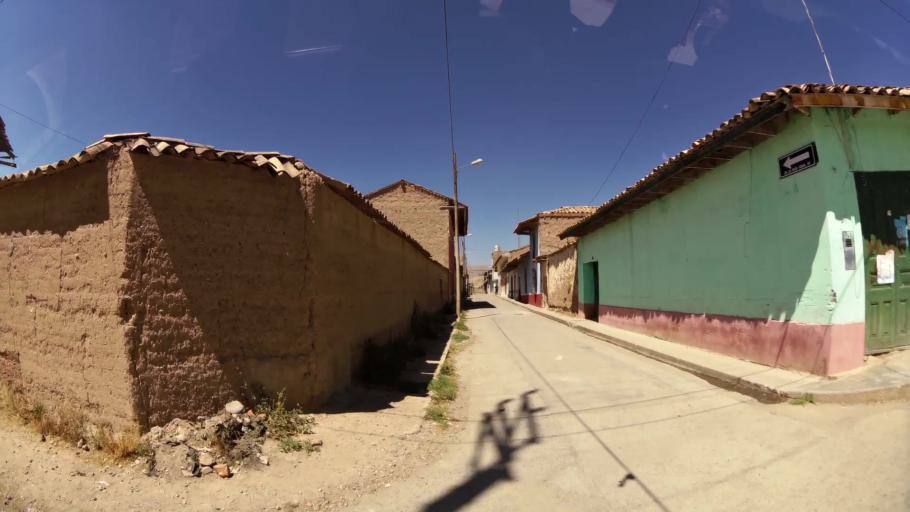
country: PE
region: Junin
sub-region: Provincia de Jauja
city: Jauja
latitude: -11.7741
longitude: -75.5028
